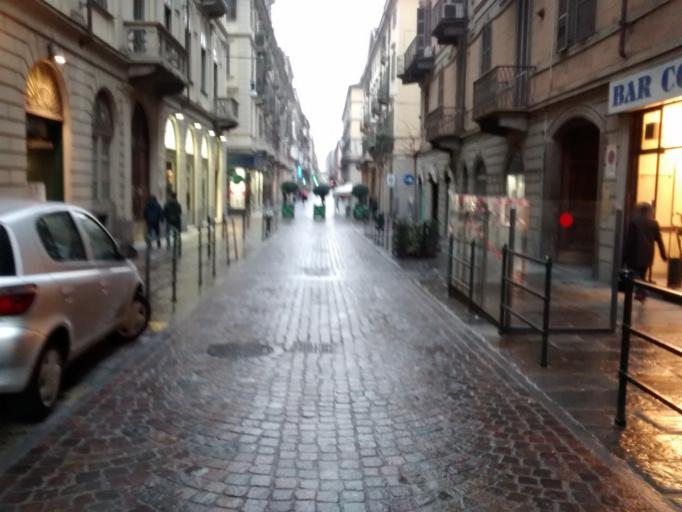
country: IT
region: Piedmont
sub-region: Provincia di Torino
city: Turin
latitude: 45.0630
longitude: 7.6825
